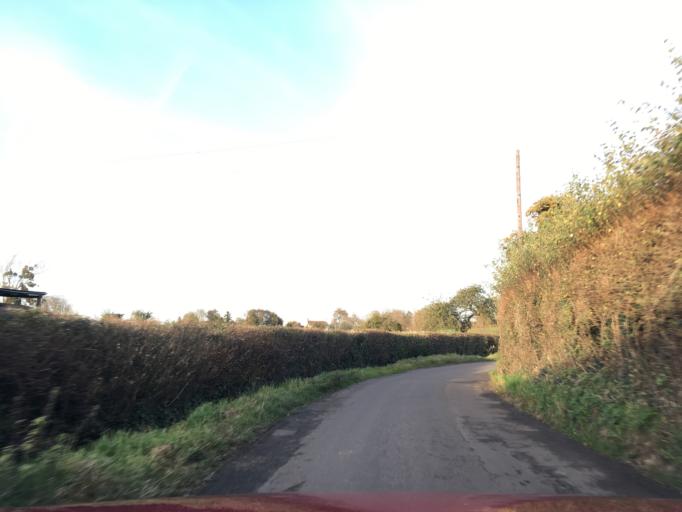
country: GB
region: England
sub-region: South Gloucestershire
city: Thornbury
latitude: 51.6246
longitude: -2.5178
